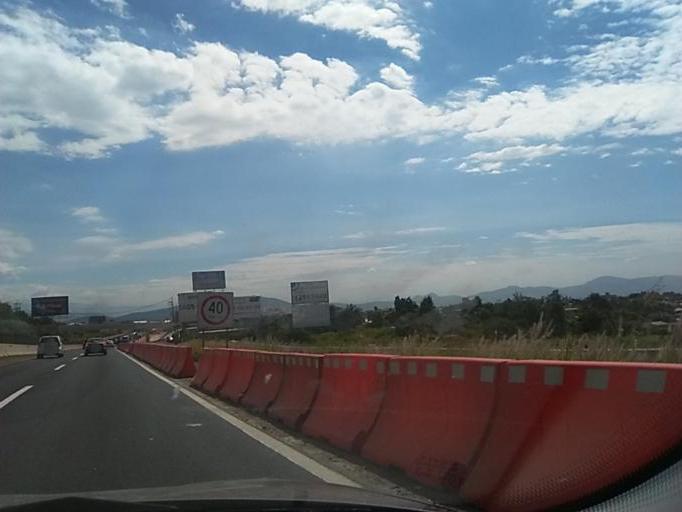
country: MX
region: Morelos
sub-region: Cuernavaca
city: Colonia los Cerritos
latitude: 18.9601
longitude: -99.2152
